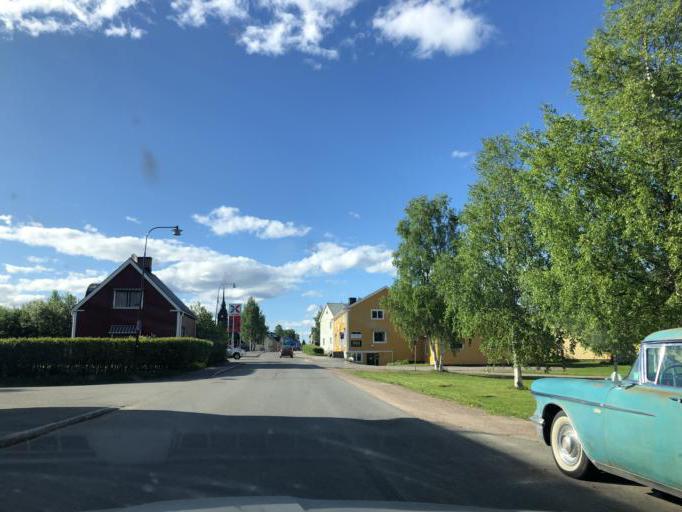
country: SE
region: Norrbotten
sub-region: Overkalix Kommun
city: OEverkalix
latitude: 66.3238
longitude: 22.8475
